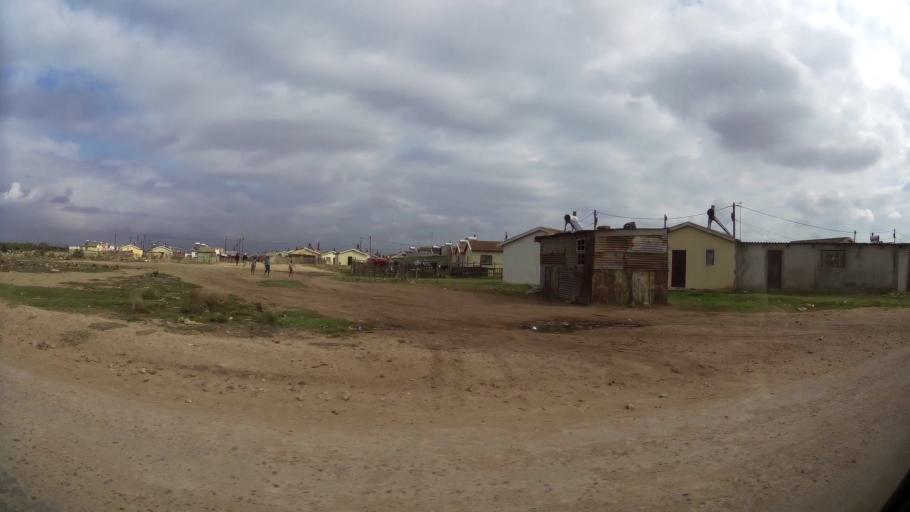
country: ZA
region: Eastern Cape
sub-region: Nelson Mandela Bay Metropolitan Municipality
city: Port Elizabeth
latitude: -33.8281
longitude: 25.6251
